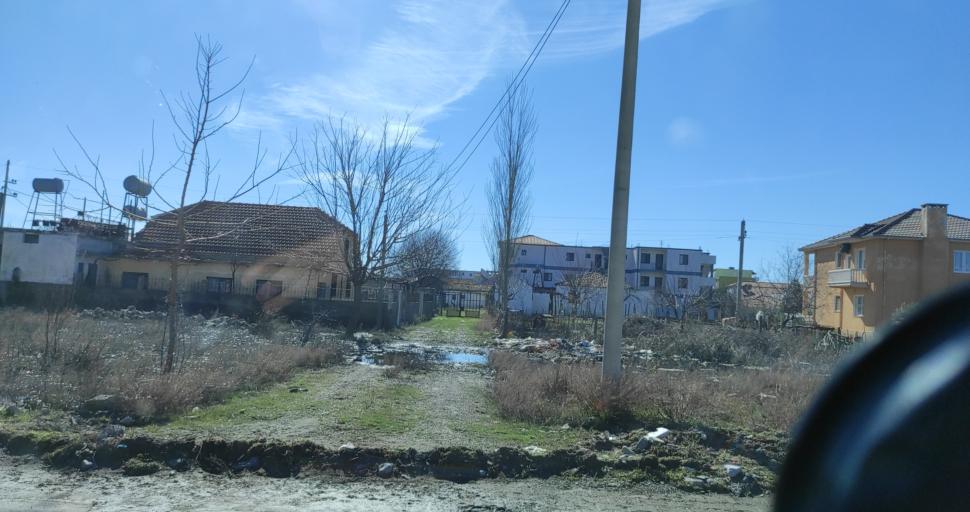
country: AL
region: Shkoder
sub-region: Rrethi i Shkodres
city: Velipoje
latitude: 41.8654
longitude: 19.4367
